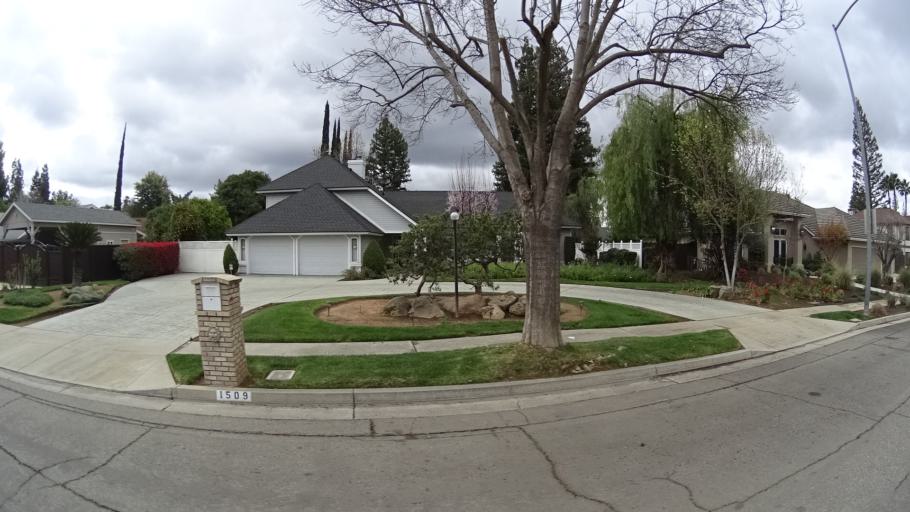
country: US
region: California
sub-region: Fresno County
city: Fresno
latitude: 36.8445
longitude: -119.8204
